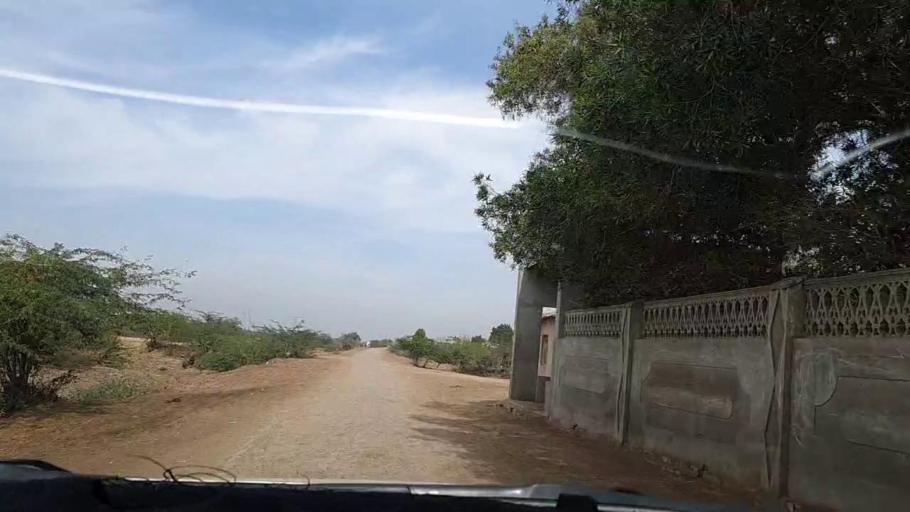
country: PK
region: Sindh
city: Dhoro Naro
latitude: 25.4523
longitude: 69.4925
